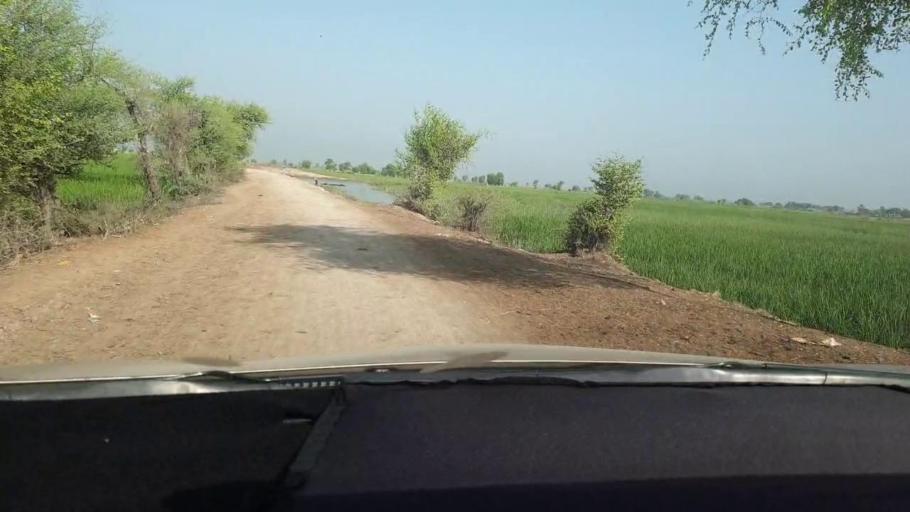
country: PK
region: Sindh
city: Miro Khan
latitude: 27.7559
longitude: 68.1413
